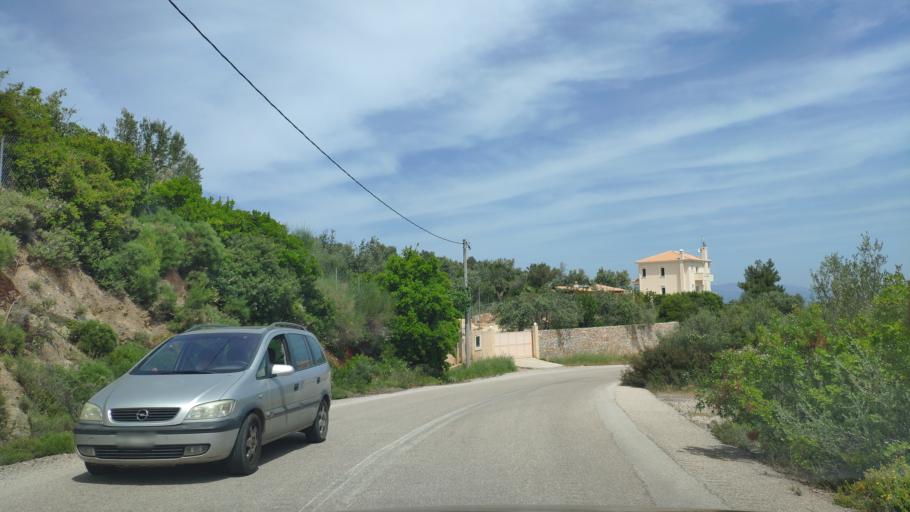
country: GR
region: Attica
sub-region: Nomarchia Anatolikis Attikis
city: Grammatiko
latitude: 38.2521
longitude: 23.9687
